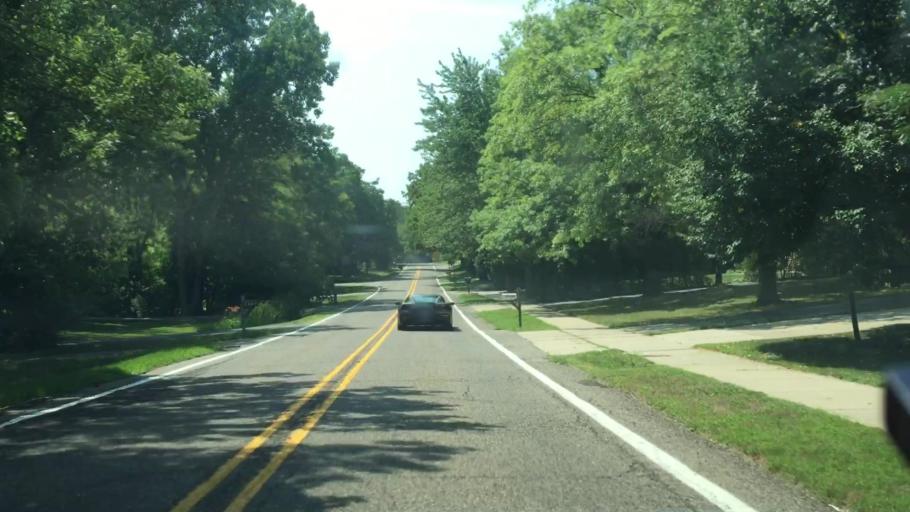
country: US
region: Michigan
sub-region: Oakland County
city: Franklin
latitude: 42.5582
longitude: -83.3168
